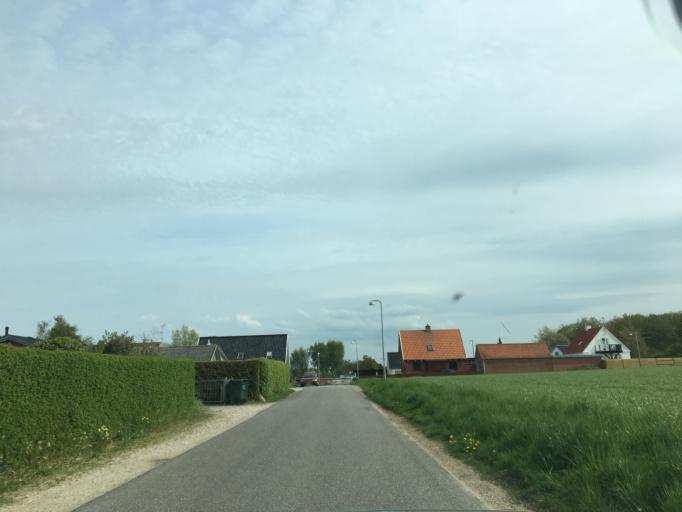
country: DK
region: Zealand
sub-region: Lejre Kommune
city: Osted
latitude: 55.5535
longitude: 11.9489
